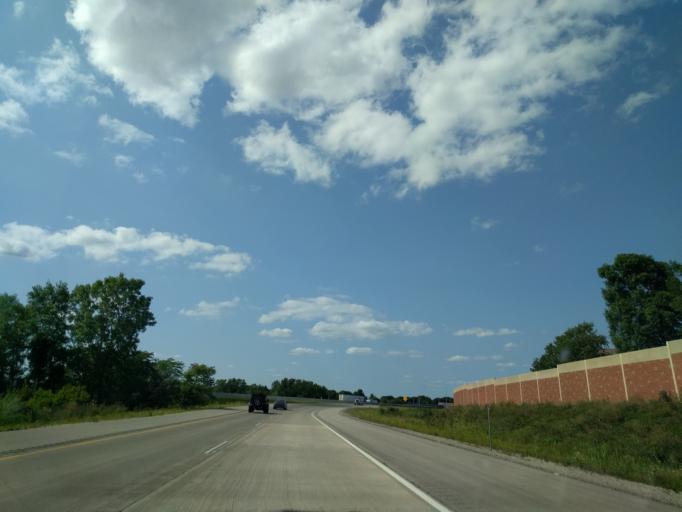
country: US
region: Wisconsin
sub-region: Brown County
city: Ashwaubenon
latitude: 44.4848
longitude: -88.0785
